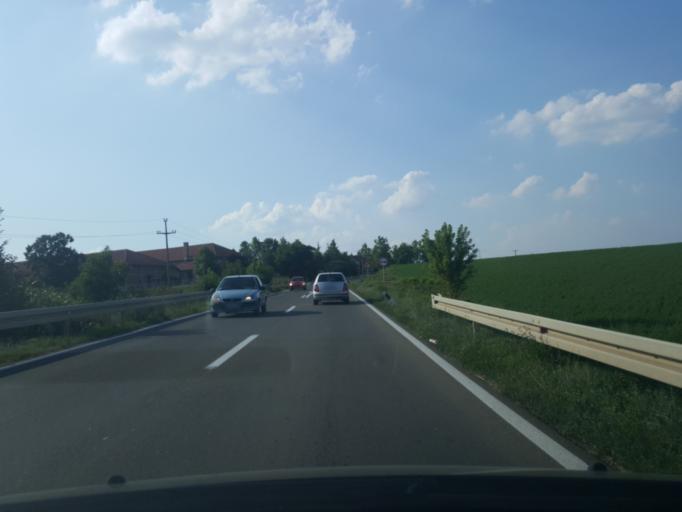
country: RS
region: Central Serbia
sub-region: Belgrade
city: Mladenovac
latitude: 44.3961
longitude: 20.6688
